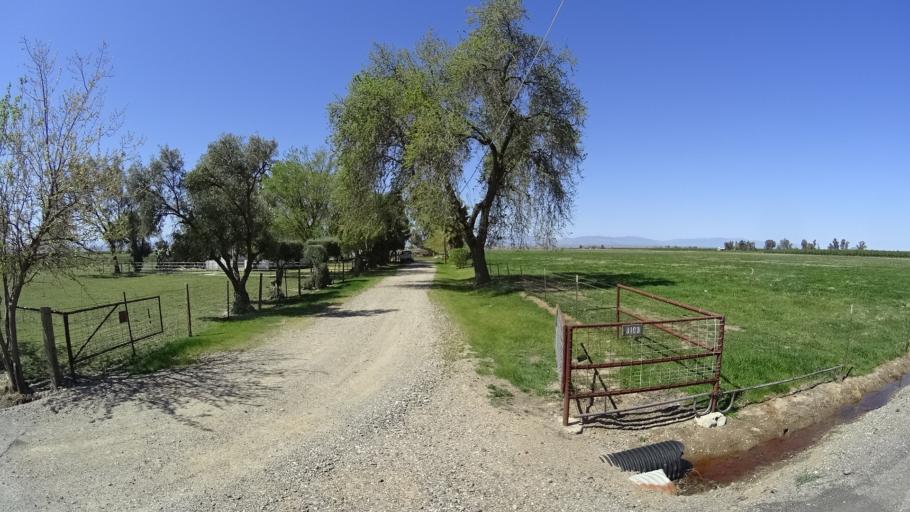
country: US
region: California
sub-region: Glenn County
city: Willows
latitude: 39.6333
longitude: -122.2347
